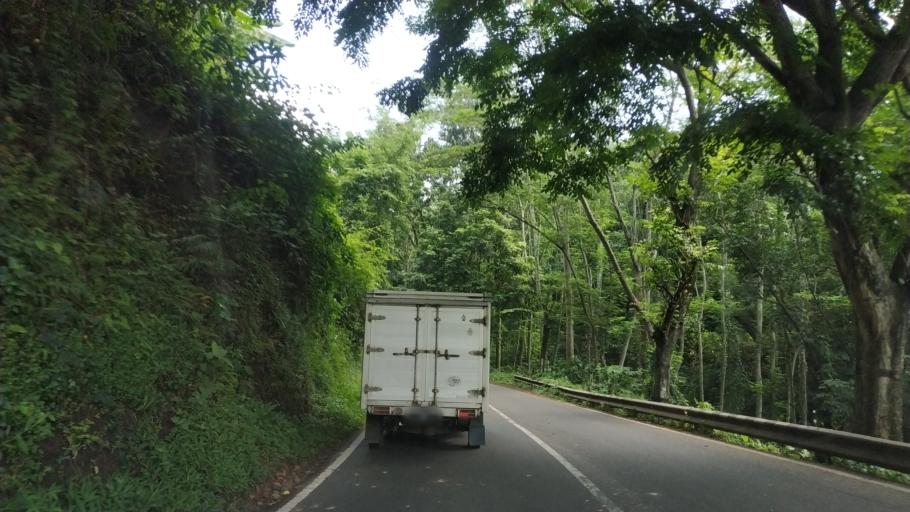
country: ID
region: Central Java
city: Weleri
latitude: -7.0005
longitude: 110.0640
